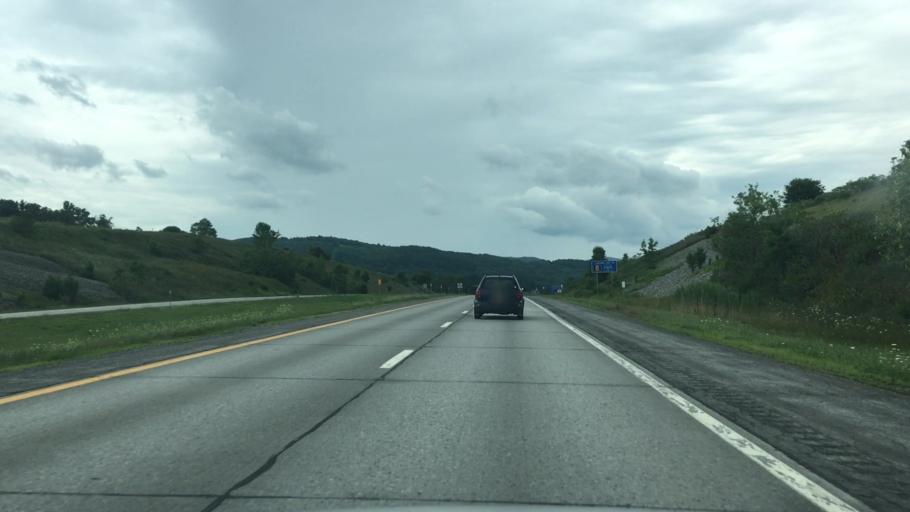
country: US
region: New York
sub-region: Schoharie County
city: Cobleskill
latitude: 42.6631
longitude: -74.4959
